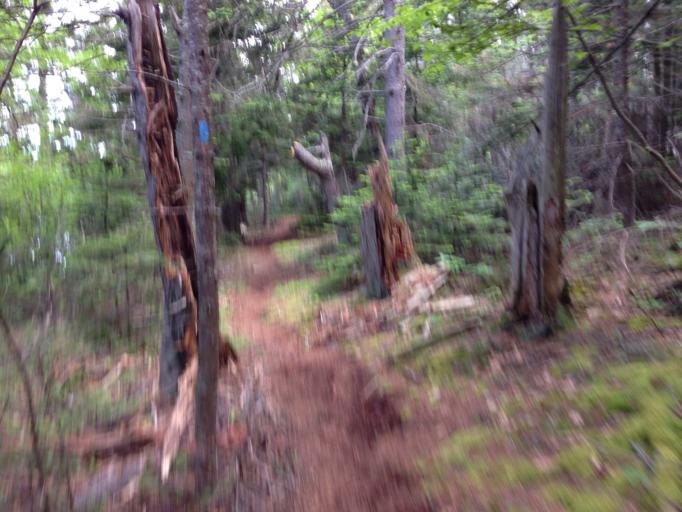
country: US
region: Maine
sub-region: Hancock County
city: Gouldsboro
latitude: 44.3805
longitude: -68.0715
